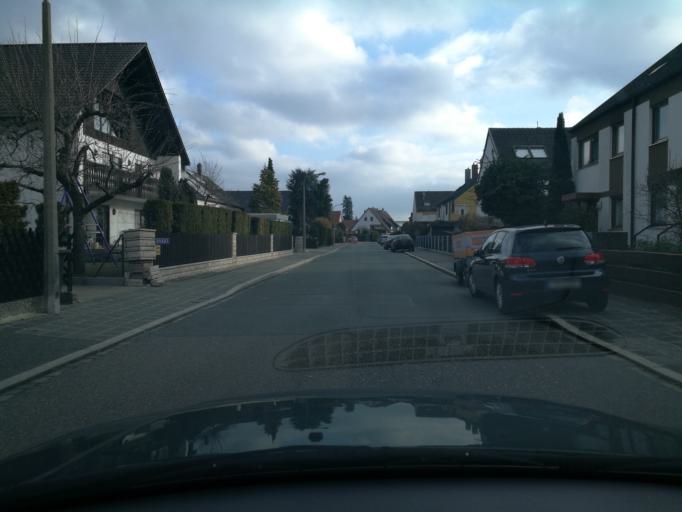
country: DE
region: Bavaria
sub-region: Regierungsbezirk Mittelfranken
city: Grossreuth bei Schweinau
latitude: 49.4543
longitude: 11.0241
